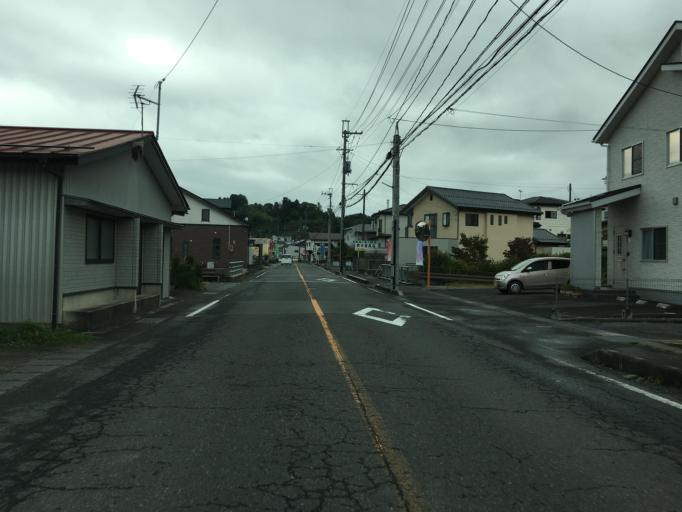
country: JP
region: Fukushima
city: Nihommatsu
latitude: 37.6026
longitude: 140.4443
